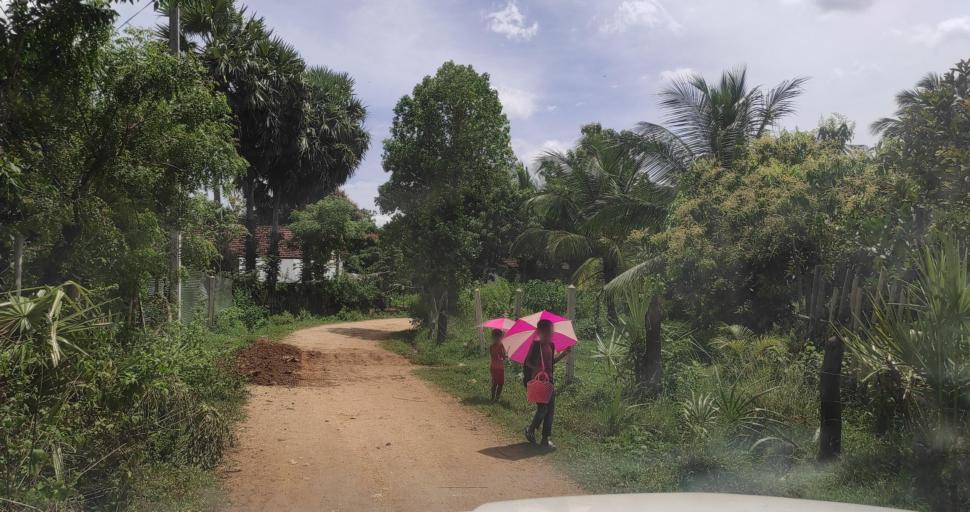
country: LK
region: Eastern Province
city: Trincomalee
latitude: 8.4417
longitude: 81.0491
